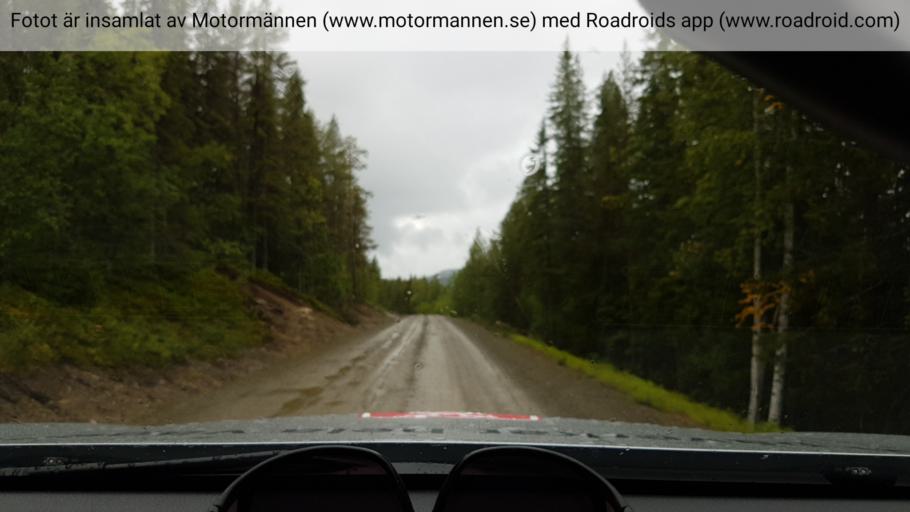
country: SE
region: Vaesterbotten
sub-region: Storumans Kommun
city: Storuman
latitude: 64.9565
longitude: 17.5695
